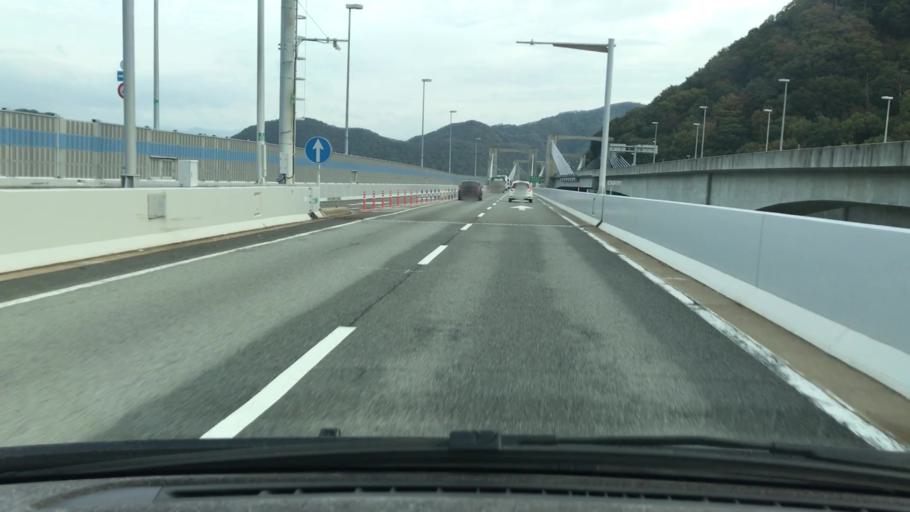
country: JP
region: Hyogo
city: Kobe
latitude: 34.7840
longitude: 135.2188
